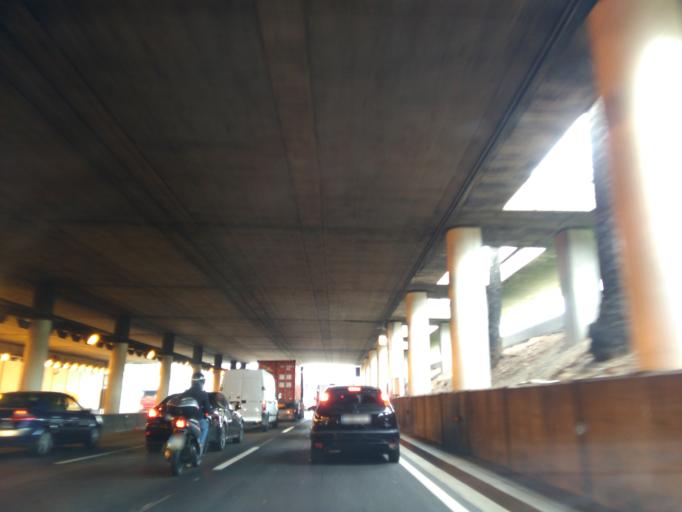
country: ES
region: Catalonia
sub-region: Provincia de Barcelona
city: Llefia
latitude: 41.4386
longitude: 2.2088
